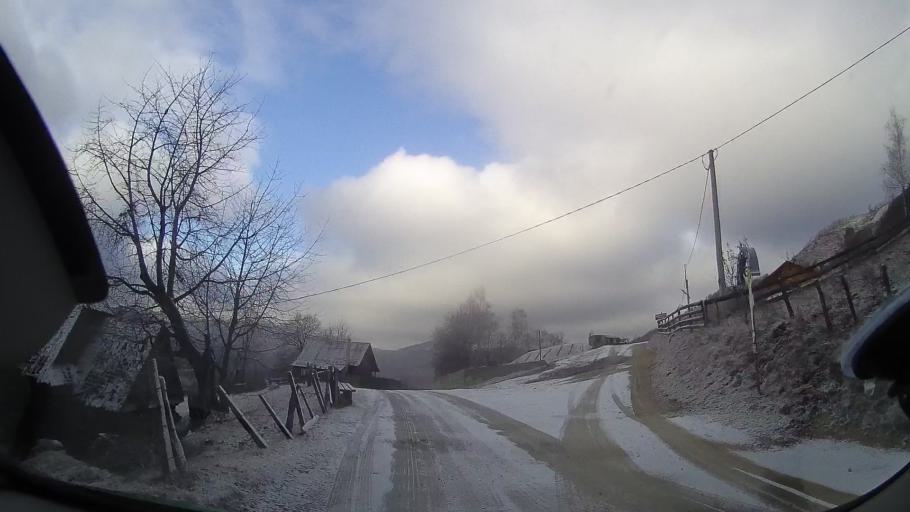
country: RO
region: Cluj
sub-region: Comuna Valea Ierii
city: Valea Ierii
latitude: 46.6728
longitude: 23.3223
